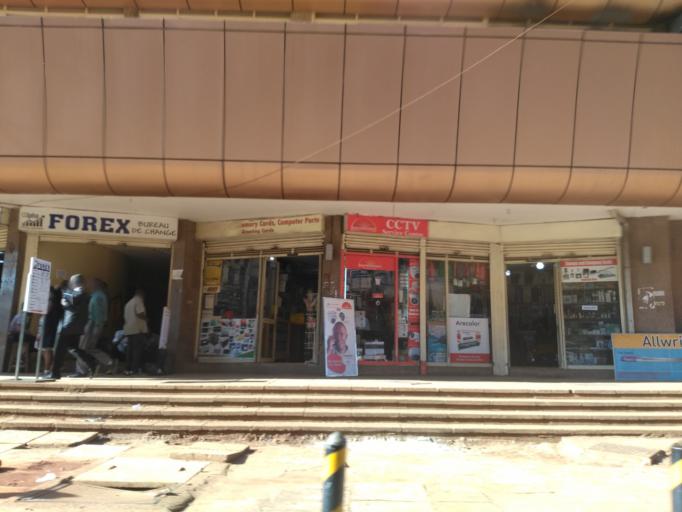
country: UG
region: Central Region
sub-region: Kampala District
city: Kampala
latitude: 0.3116
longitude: 32.5834
